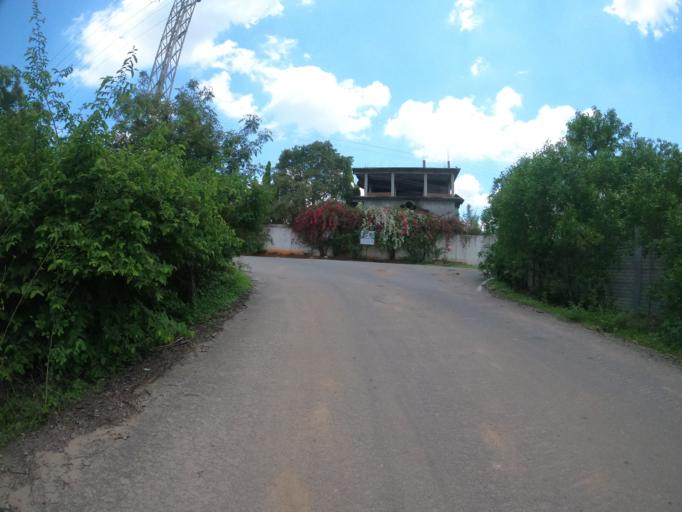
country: IN
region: Telangana
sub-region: Medak
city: Serilingampalle
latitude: 17.3714
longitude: 78.3240
